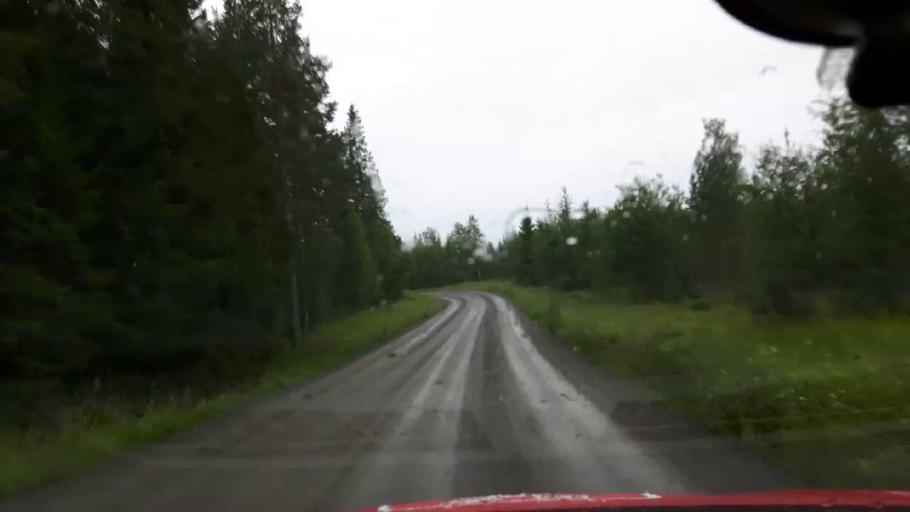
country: SE
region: Jaemtland
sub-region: OEstersunds Kommun
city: Brunflo
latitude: 62.9775
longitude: 14.8305
